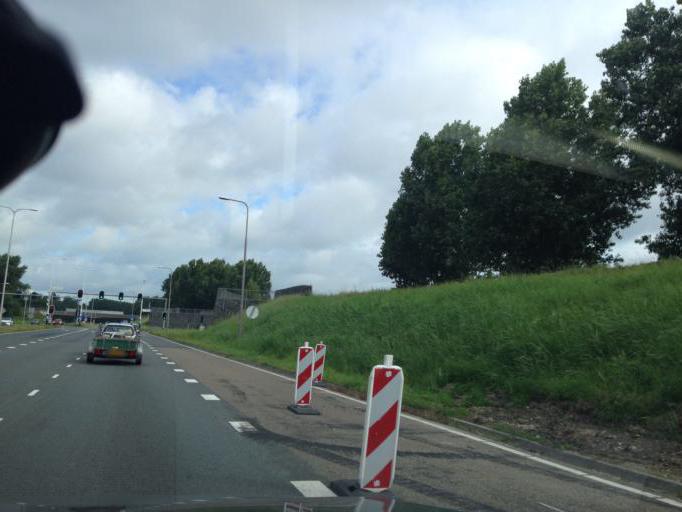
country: NL
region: Flevoland
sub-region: Gemeente Almere
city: Almere Stad
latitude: 52.3554
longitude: 5.1732
